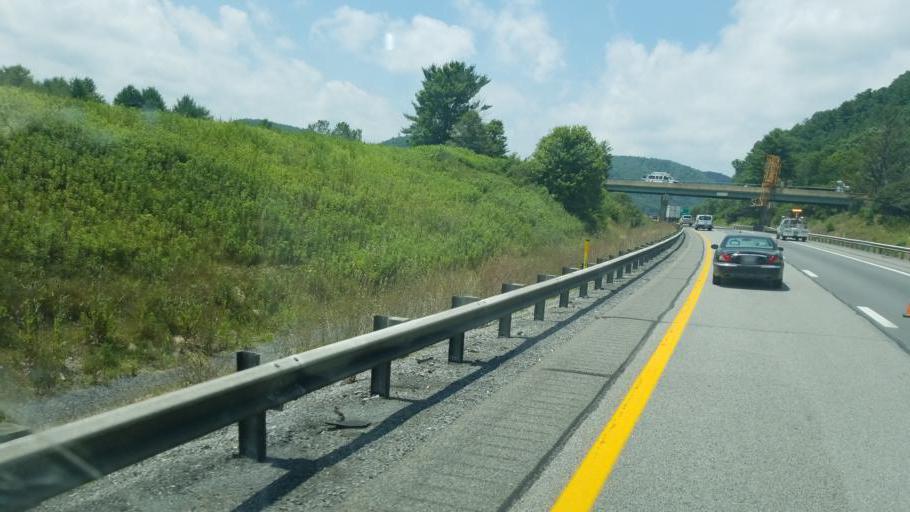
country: US
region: West Virginia
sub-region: Mercer County
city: Athens
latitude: 37.4932
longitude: -81.0928
